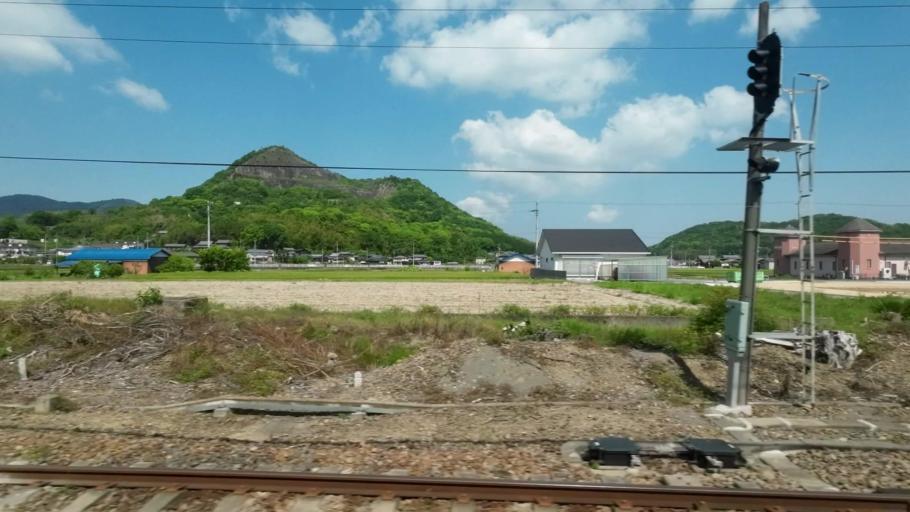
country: JP
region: Kagawa
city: Kan'onjicho
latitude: 34.1849
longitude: 133.7119
